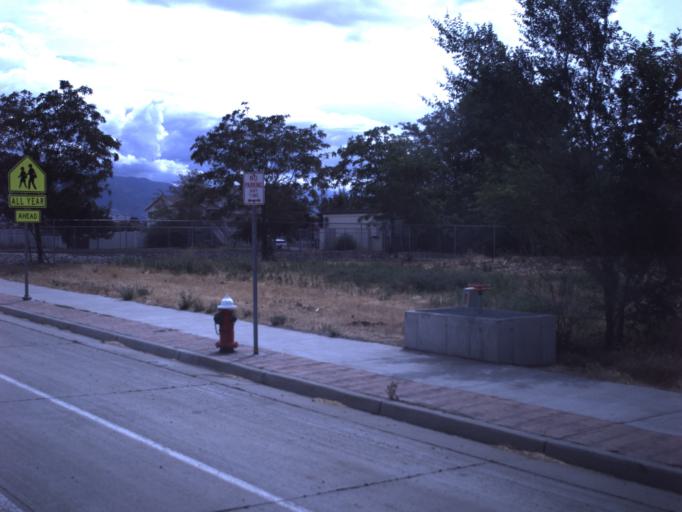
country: US
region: Utah
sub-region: Davis County
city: Syracuse
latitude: 41.0890
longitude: -112.0563
